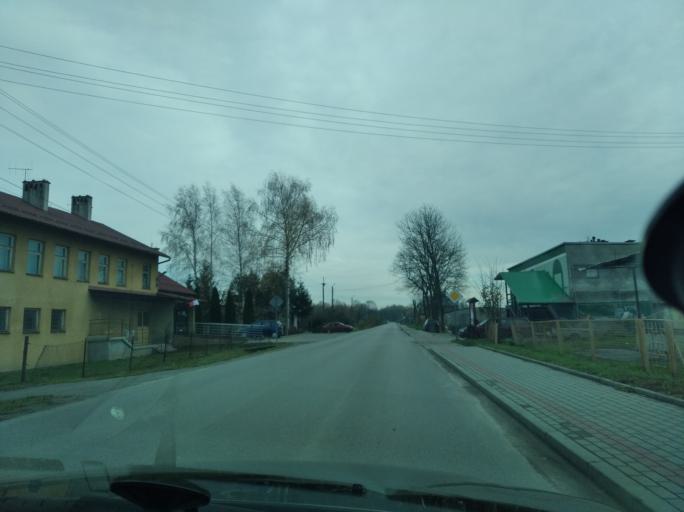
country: PL
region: Subcarpathian Voivodeship
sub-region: Powiat przeworski
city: Gac
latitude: 50.0283
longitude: 22.3728
